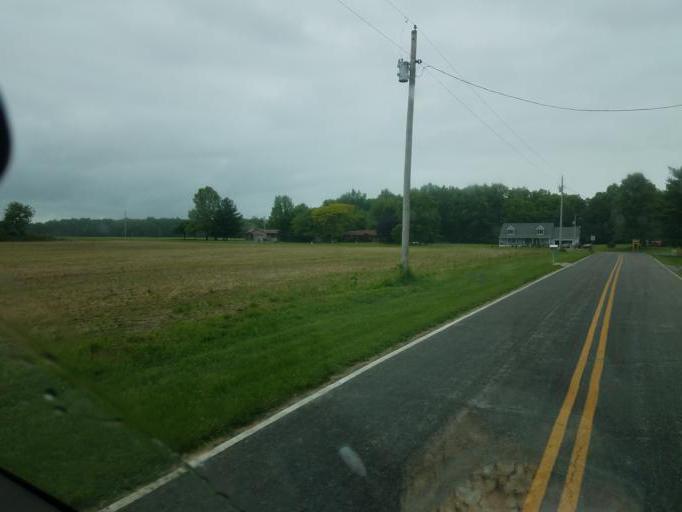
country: US
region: Ohio
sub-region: Marion County
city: Marion
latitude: 40.5522
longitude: -83.0177
